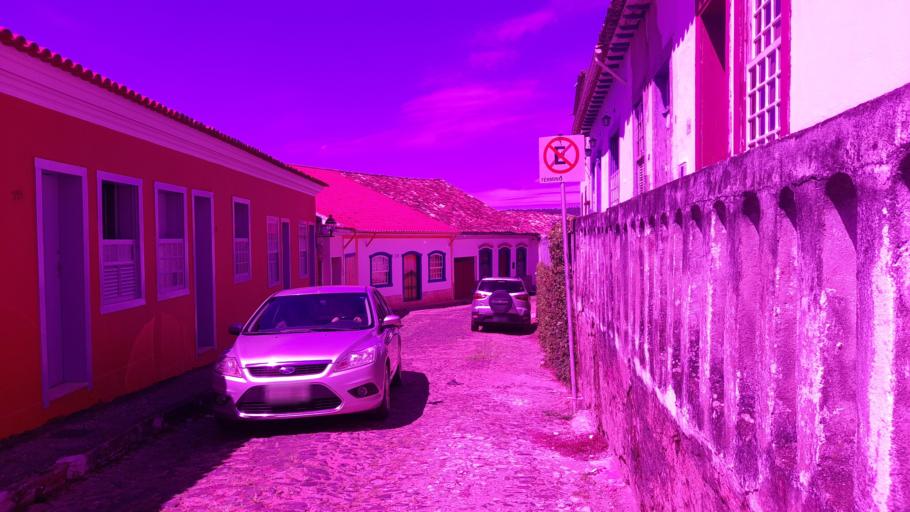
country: BR
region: Minas Gerais
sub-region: Sao Joao Del Rei
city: Sao Joao del Rei
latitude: -21.1370
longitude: -44.2637
